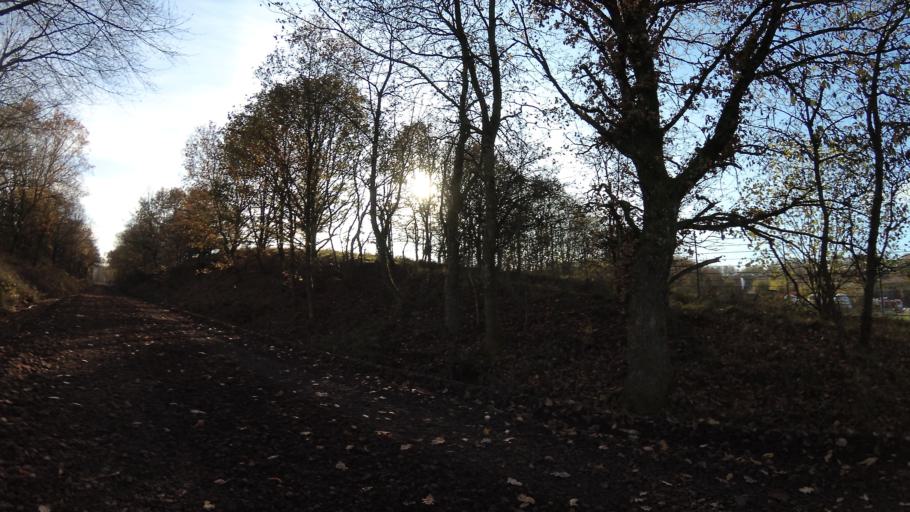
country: DE
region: Rheinland-Pfalz
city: Gimbweiler
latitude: 49.5572
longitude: 7.1751
